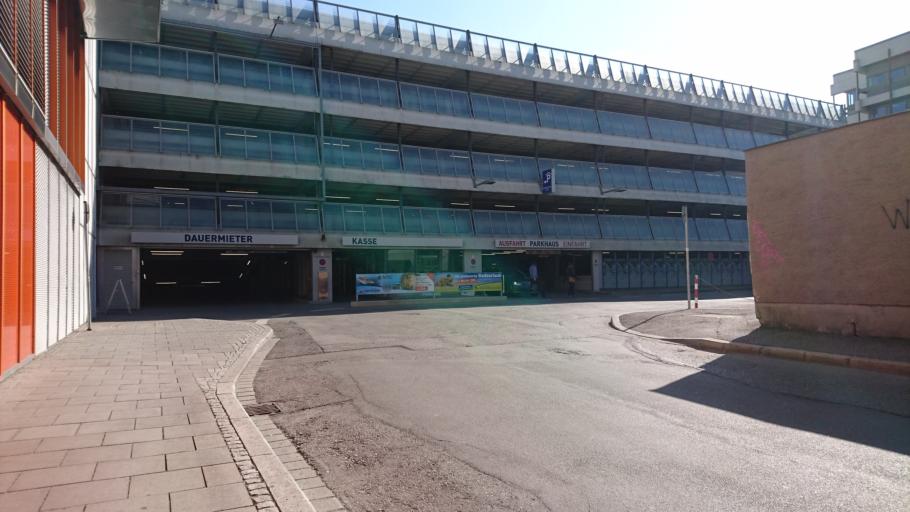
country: DE
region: Bavaria
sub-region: Swabia
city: Augsburg
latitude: 48.3692
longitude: 10.8946
